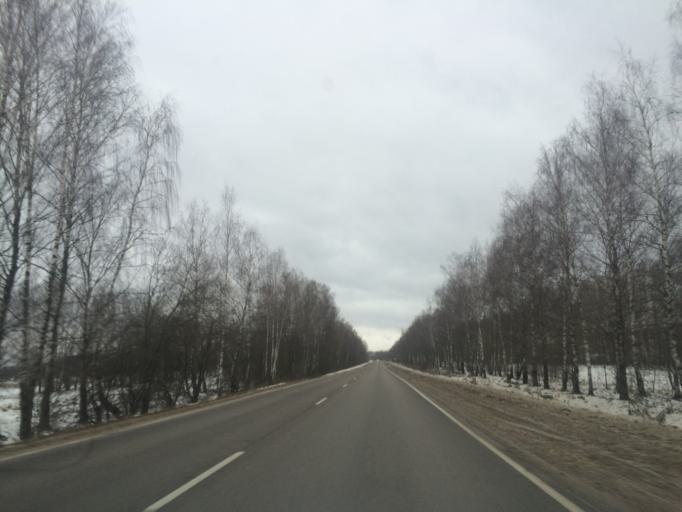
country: RU
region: Tula
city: Leninskiy
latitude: 54.1314
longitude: 37.3125
